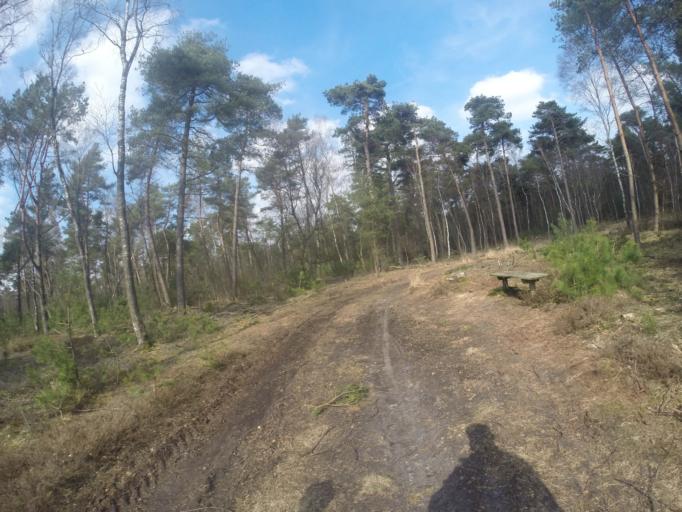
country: NL
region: Gelderland
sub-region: Gemeente Lochem
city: Almen
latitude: 52.1450
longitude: 6.3258
